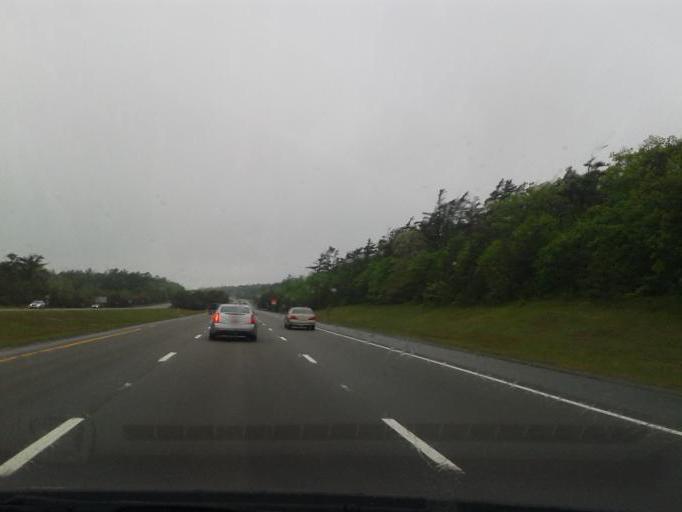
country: US
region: Massachusetts
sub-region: Plymouth County
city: White Island Shores
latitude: 41.7783
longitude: -70.6270
